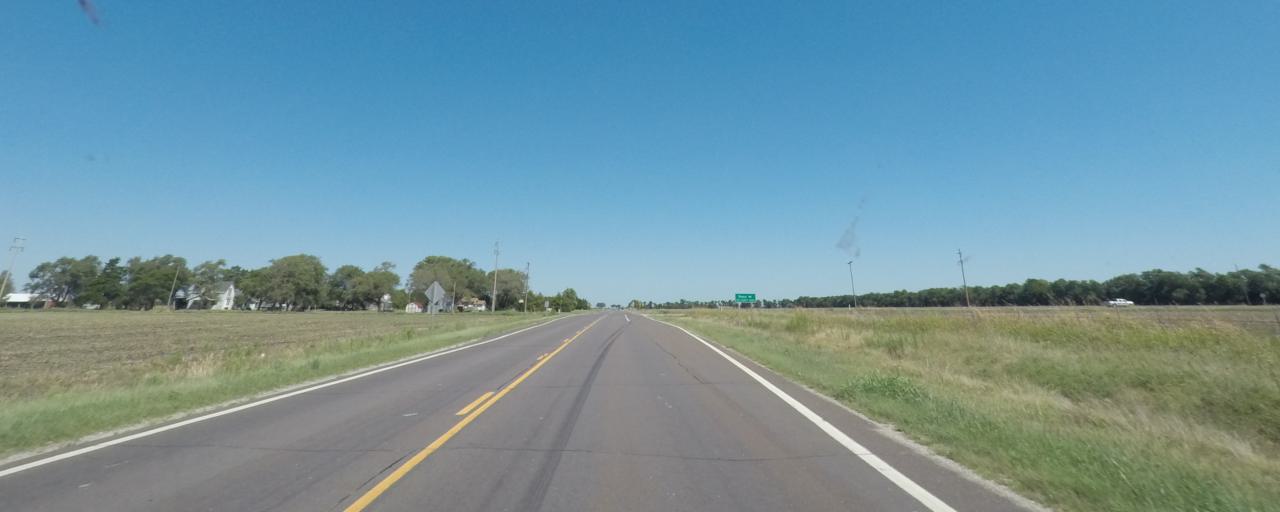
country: US
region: Kansas
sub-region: Sumner County
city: Wellington
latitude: 37.1572
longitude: -97.4023
